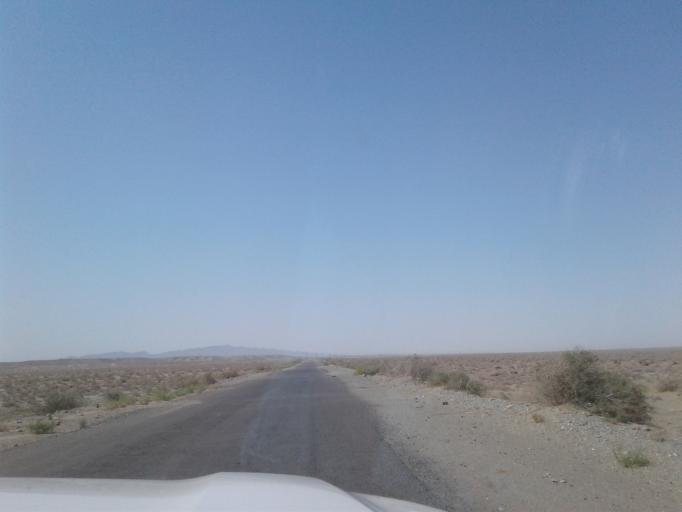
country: TM
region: Balkan
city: Gazanjyk
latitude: 39.2591
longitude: 55.3131
